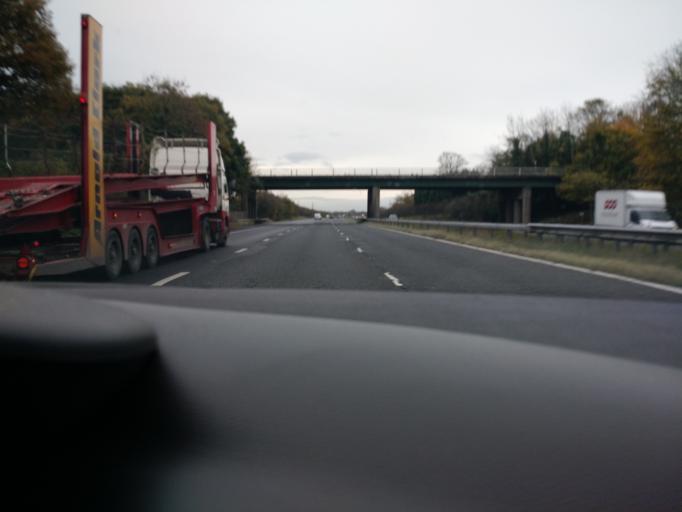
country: GB
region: England
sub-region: Lancashire
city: Preston
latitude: 53.8018
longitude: -2.7860
